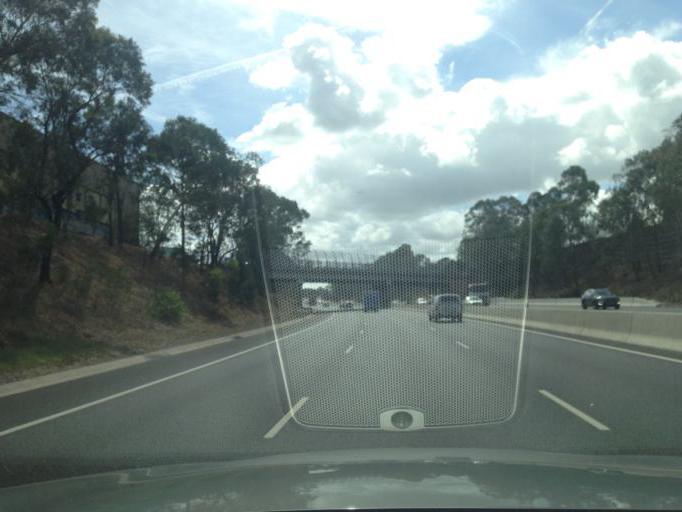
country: AU
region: New South Wales
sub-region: Bankstown
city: Milperra
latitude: -33.9432
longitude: 150.9988
